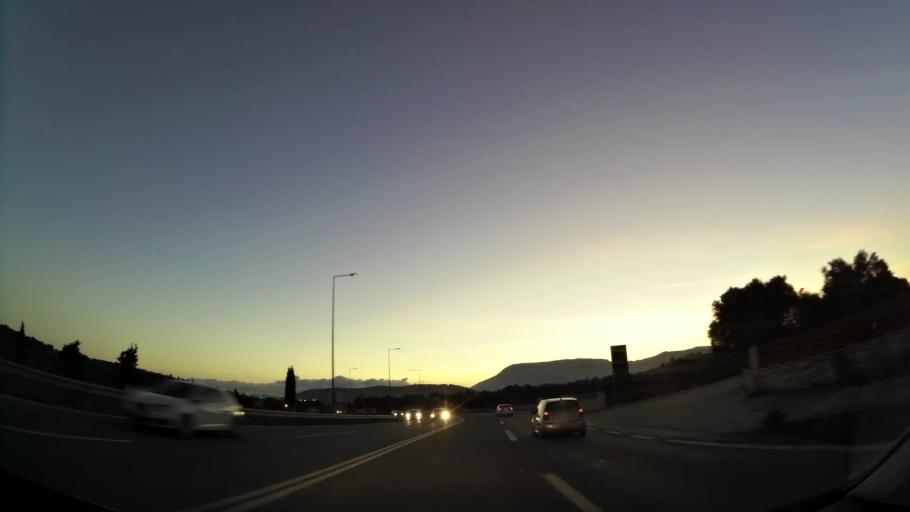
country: GR
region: Attica
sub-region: Nomarchia Anatolikis Attikis
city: Pikermi
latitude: 37.9953
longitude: 23.9219
